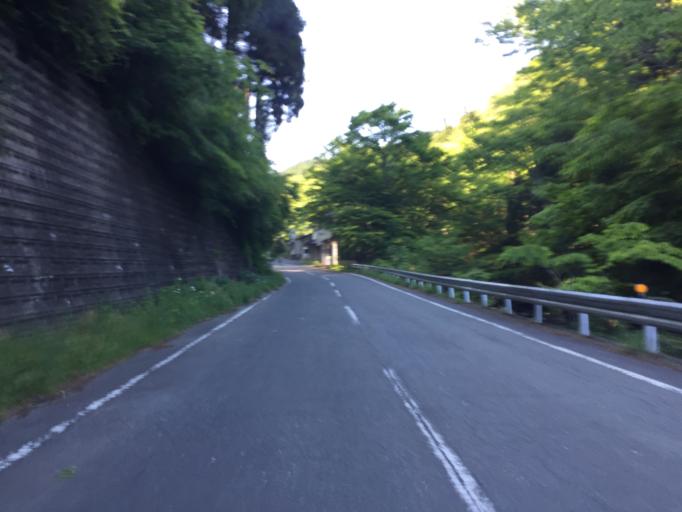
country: JP
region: Ibaraki
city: Kitaibaraki
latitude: 36.8670
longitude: 140.6368
